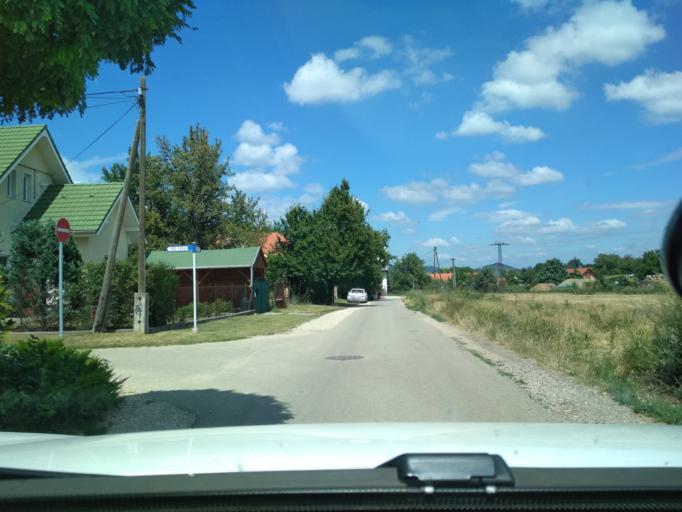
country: HU
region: Fejer
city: Velence
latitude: 47.2160
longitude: 18.6613
